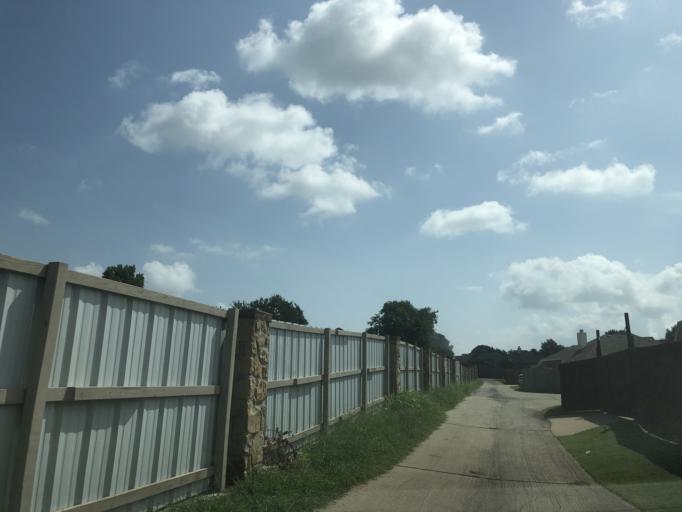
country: US
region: Texas
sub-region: Dallas County
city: Sunnyvale
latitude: 32.8350
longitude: -96.5678
